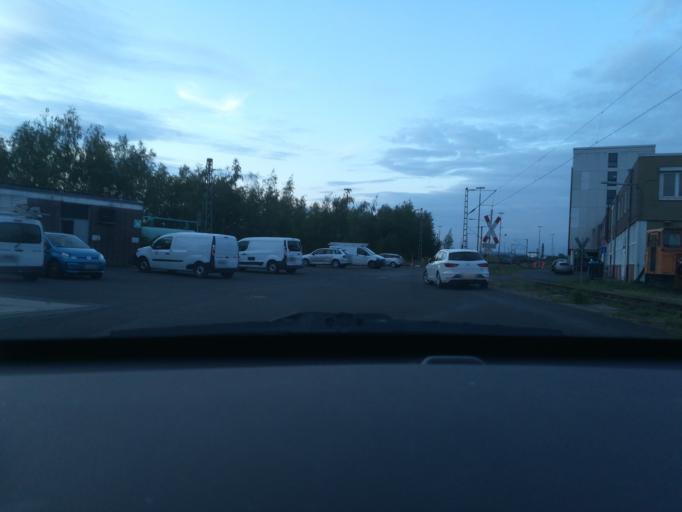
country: DE
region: Hesse
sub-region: Regierungsbezirk Kassel
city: Kassel
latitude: 51.3258
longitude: 9.4663
